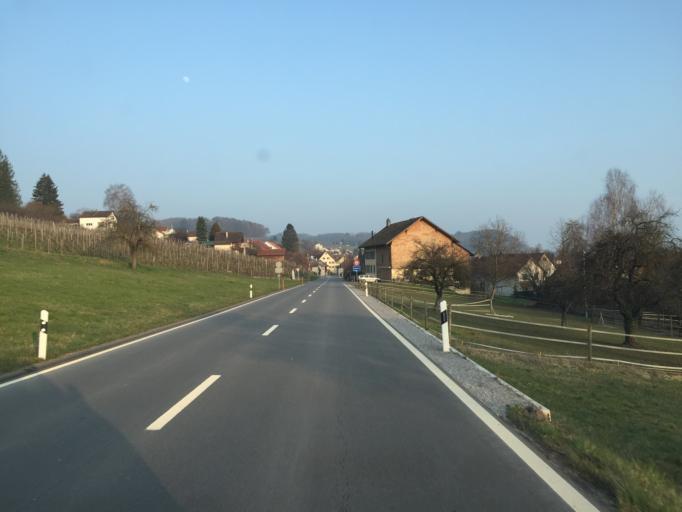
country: CH
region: Zurich
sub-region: Bezirk Andelfingen
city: Uhwiesen
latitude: 47.6548
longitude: 8.6478
